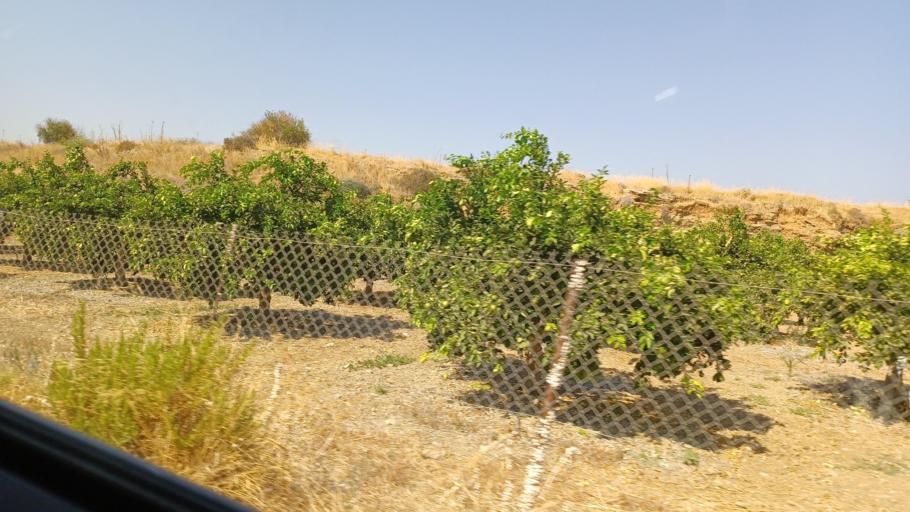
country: CY
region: Pafos
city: Polis
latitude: 35.0467
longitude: 32.4453
